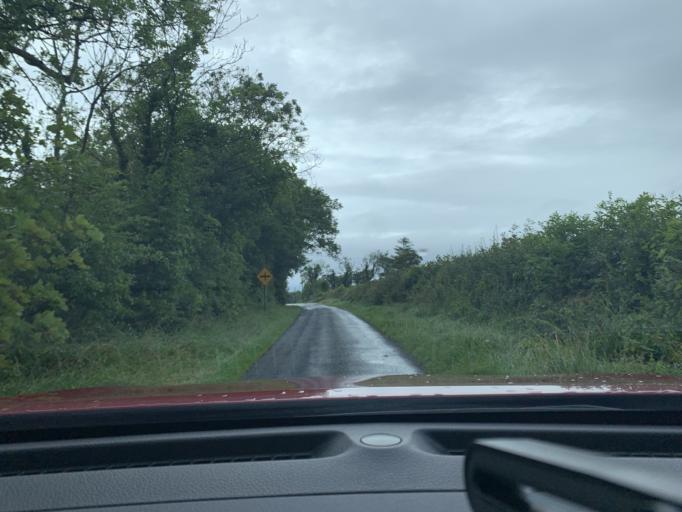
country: IE
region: Connaught
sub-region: Sligo
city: Strandhill
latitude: 54.3665
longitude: -8.5564
